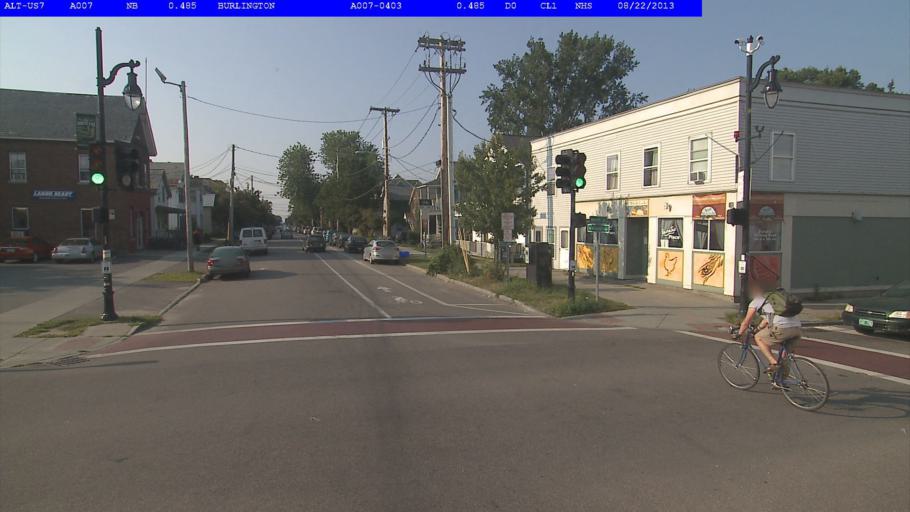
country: US
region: Vermont
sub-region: Chittenden County
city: Burlington
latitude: 44.4849
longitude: -73.2114
